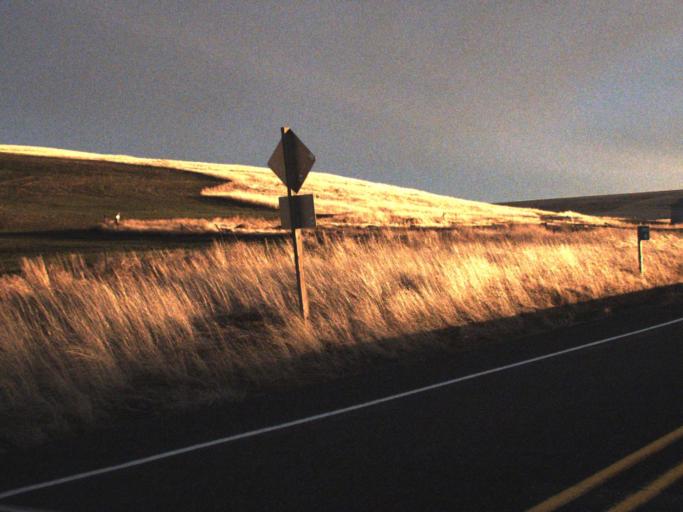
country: US
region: Washington
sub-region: Garfield County
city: Pomeroy
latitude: 46.5786
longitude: -117.7756
